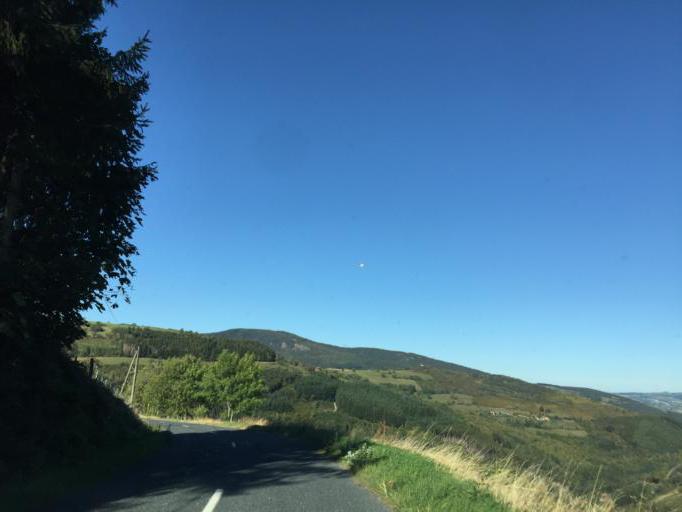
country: FR
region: Rhone-Alpes
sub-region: Departement de la Loire
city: Saint-Chamond
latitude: 45.4079
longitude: 4.5450
